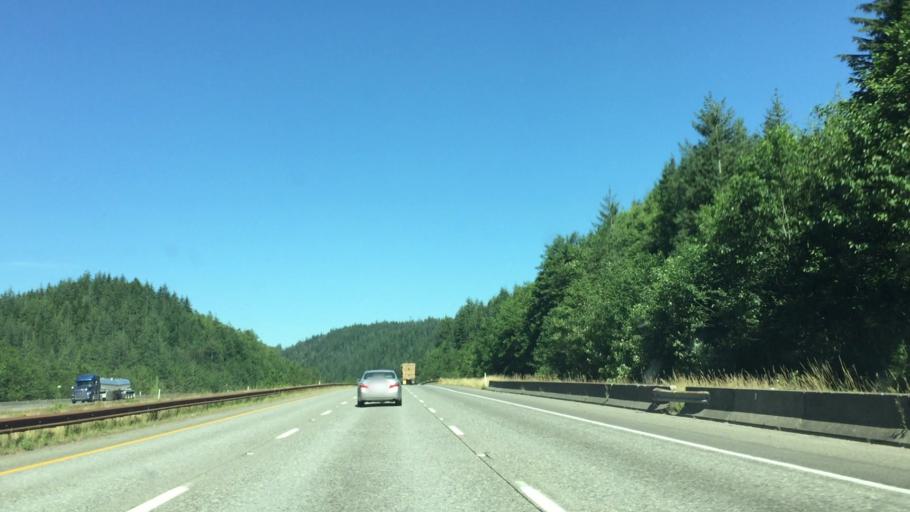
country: US
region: Washington
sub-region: King County
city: Tanner
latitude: 47.4373
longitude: -121.6474
